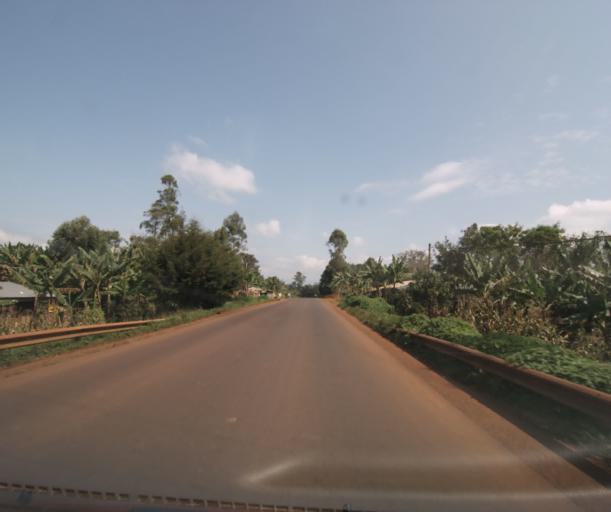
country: CM
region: West
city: Bansoa
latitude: 5.4870
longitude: 10.2677
